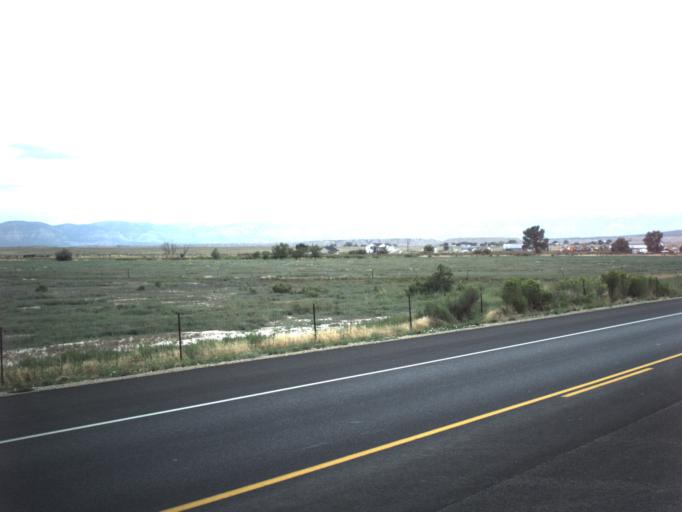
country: US
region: Utah
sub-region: Carbon County
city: Wellington
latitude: 39.5425
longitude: -110.7161
